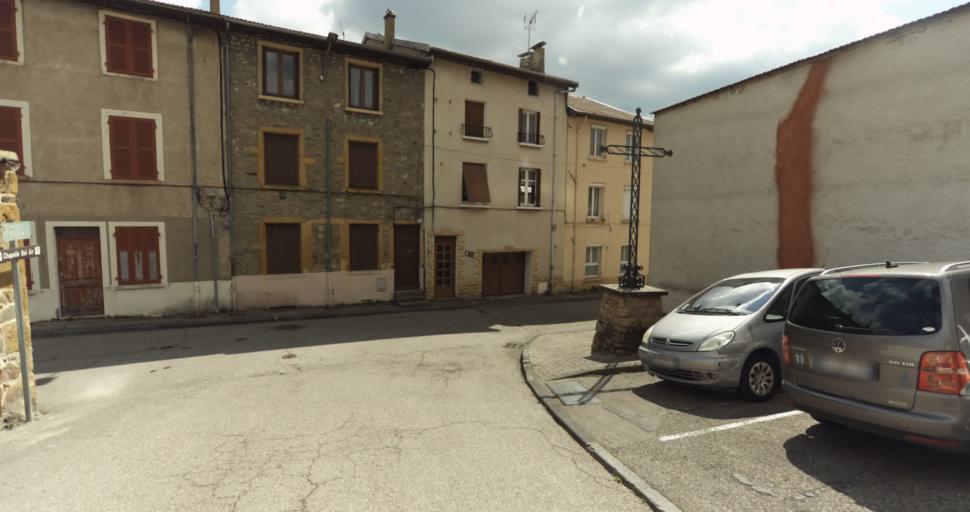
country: FR
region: Rhone-Alpes
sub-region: Departement du Rhone
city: Tarare
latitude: 45.8989
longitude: 4.4305
